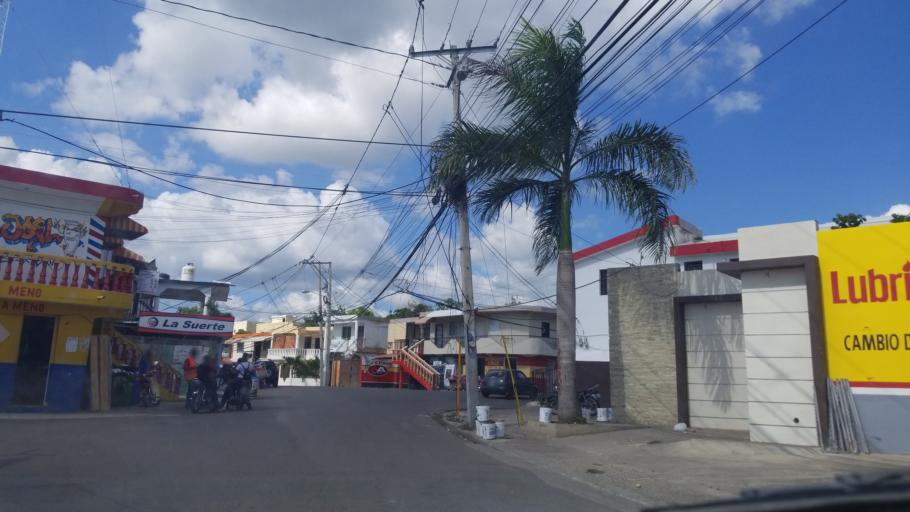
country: DO
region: Santiago
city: Santiago de los Caballeros
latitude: 19.4788
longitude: -70.6886
